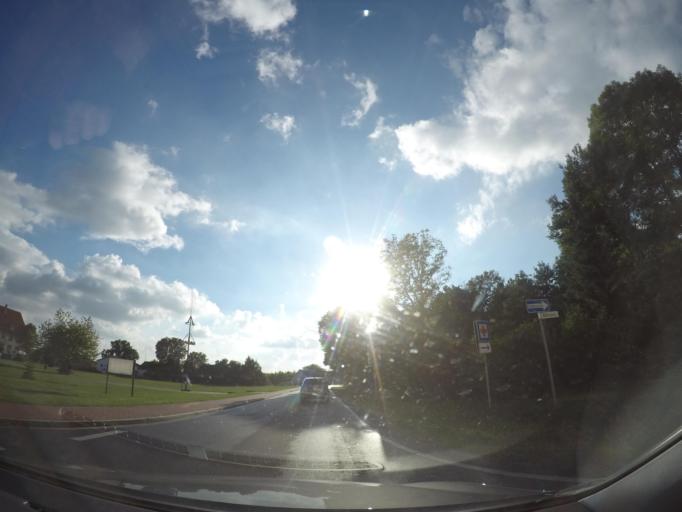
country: DE
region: Lower Saxony
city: Mariental
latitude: 52.2900
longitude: 10.9953
